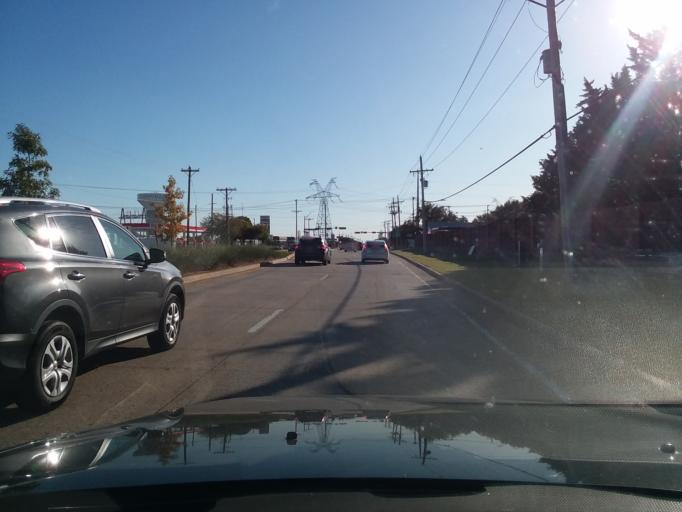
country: US
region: Texas
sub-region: Denton County
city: Highland Village
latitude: 33.0714
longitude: -97.0377
